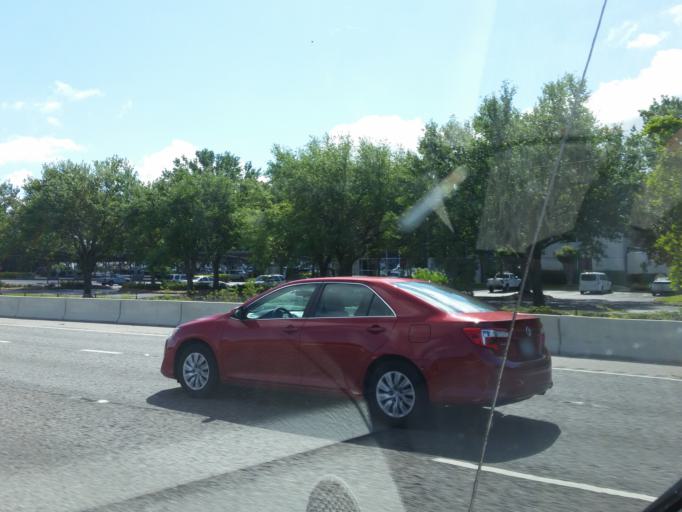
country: US
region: Florida
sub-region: Orange County
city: Oak Ridge
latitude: 28.5037
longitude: -81.4241
